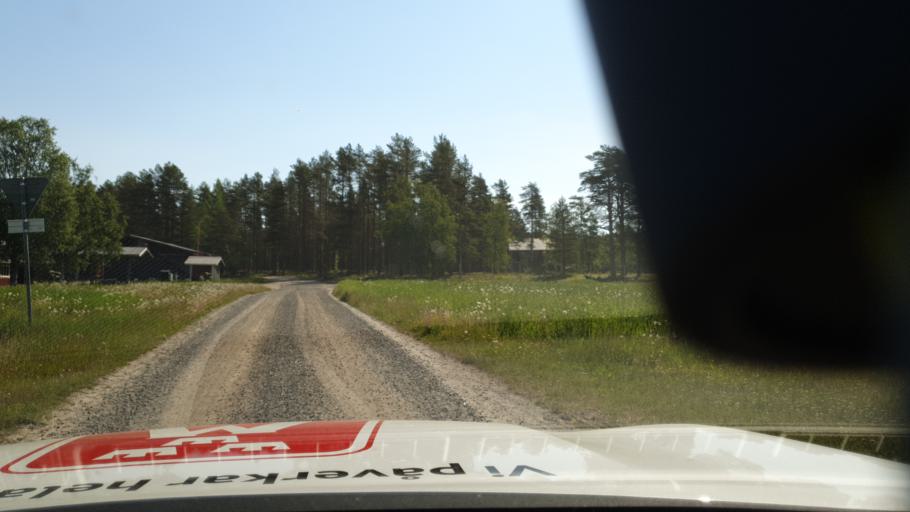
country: SE
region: Vaesterbotten
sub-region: Robertsfors Kommun
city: Robertsfors
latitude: 64.2224
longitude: 21.0178
